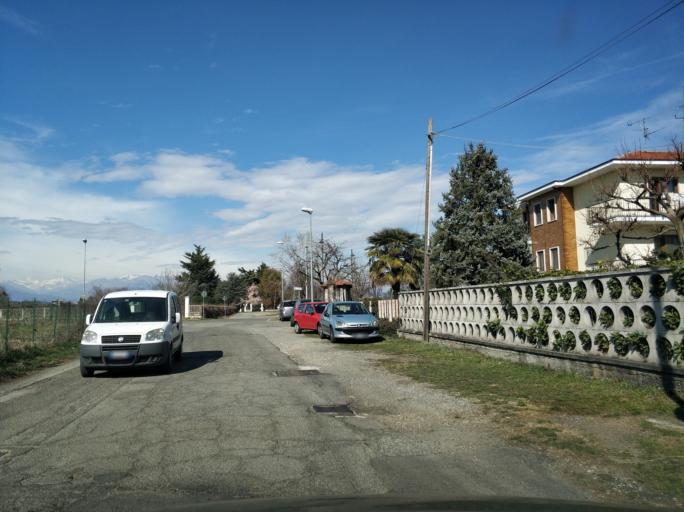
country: IT
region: Piedmont
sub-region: Provincia di Torino
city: Leini
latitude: 45.1866
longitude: 7.7083
